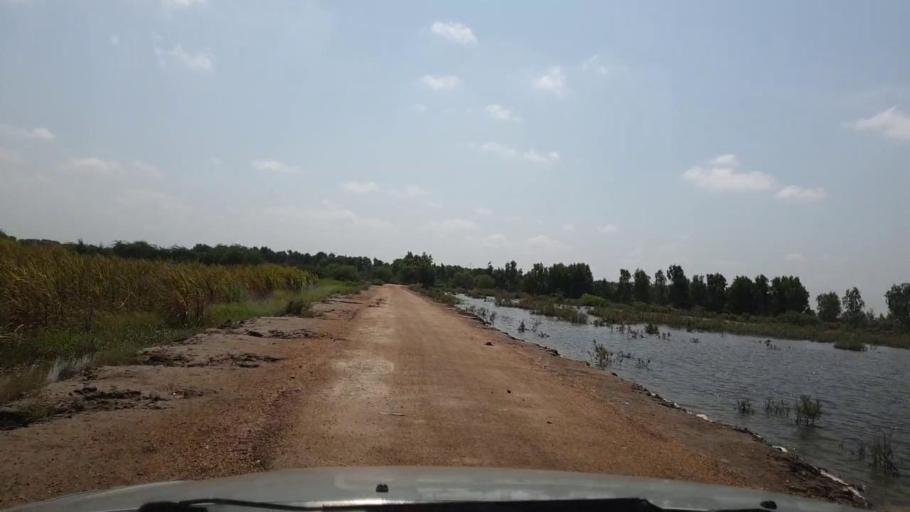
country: PK
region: Sindh
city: Rajo Khanani
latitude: 25.0137
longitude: 68.8567
